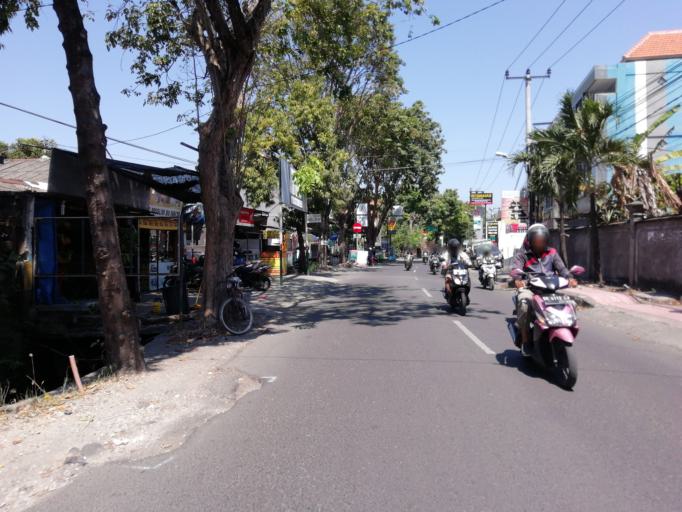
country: ID
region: Bali
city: Karyadharma
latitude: -8.6831
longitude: 115.2262
